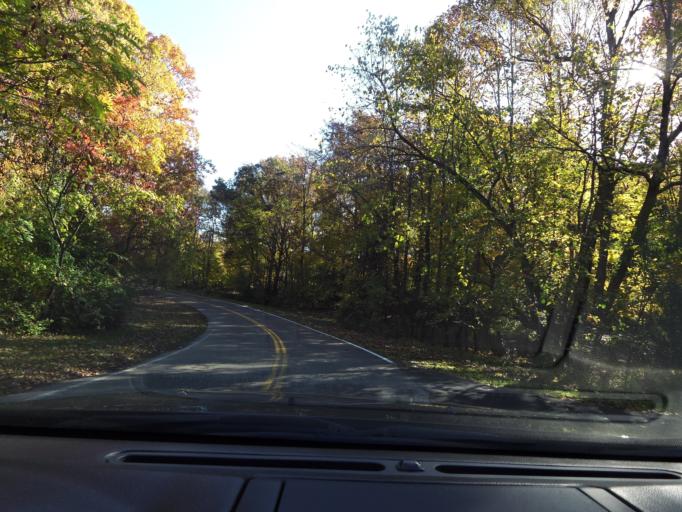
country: US
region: New York
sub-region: Wyoming County
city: Castile
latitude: 42.6176
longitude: -77.9968
